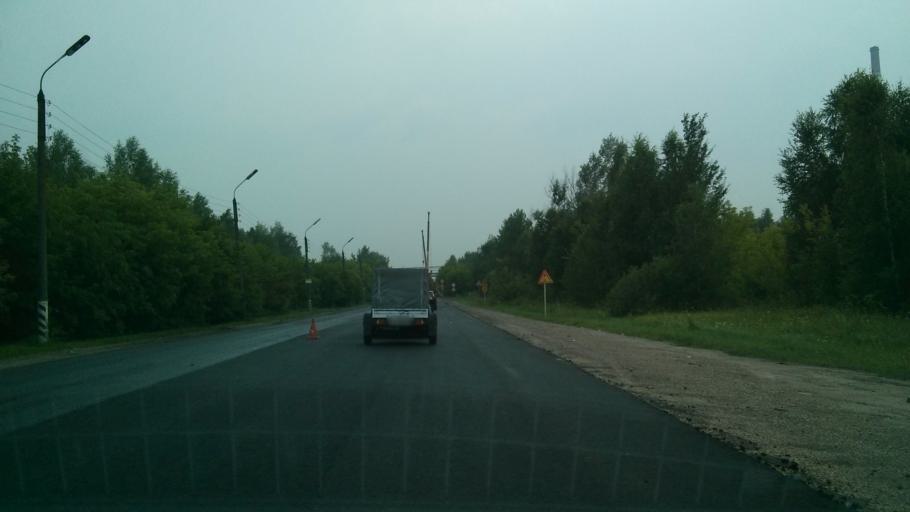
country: RU
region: Nizjnij Novgorod
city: Kstovo
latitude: 56.1126
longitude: 44.1483
